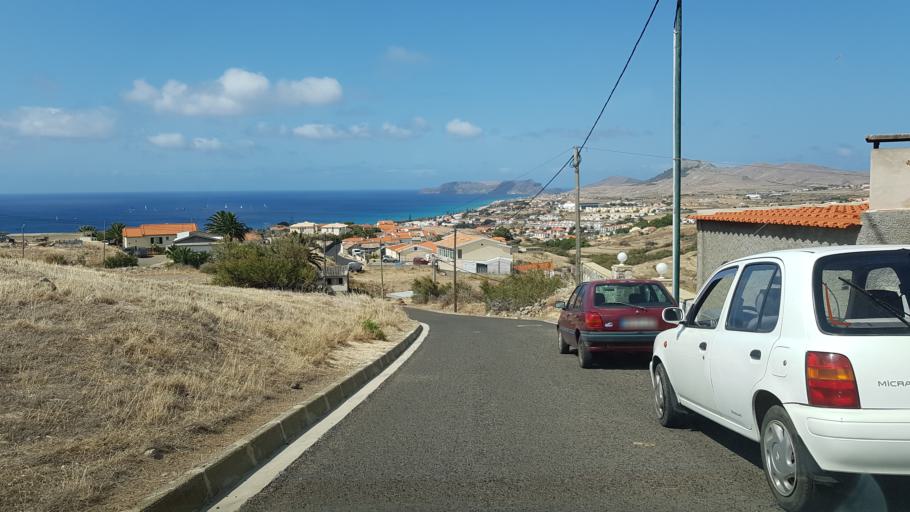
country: PT
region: Madeira
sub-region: Porto Santo
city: Vila de Porto Santo
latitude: 33.0726
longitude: -16.3253
